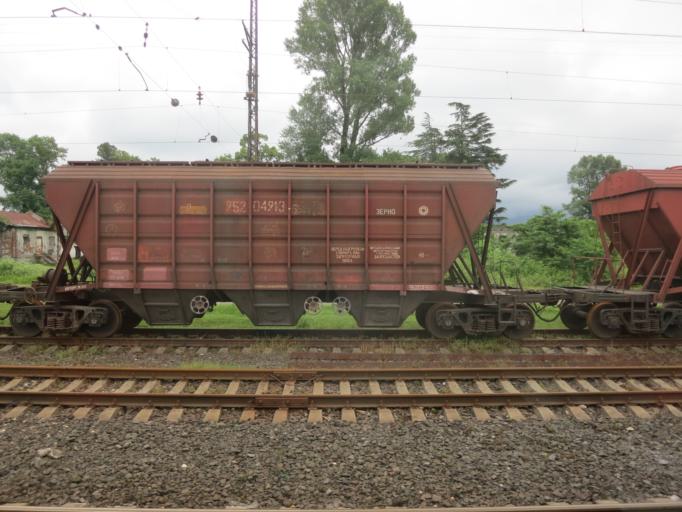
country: GE
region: Ajaria
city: Kobuleti
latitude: 41.8100
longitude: 41.7809
